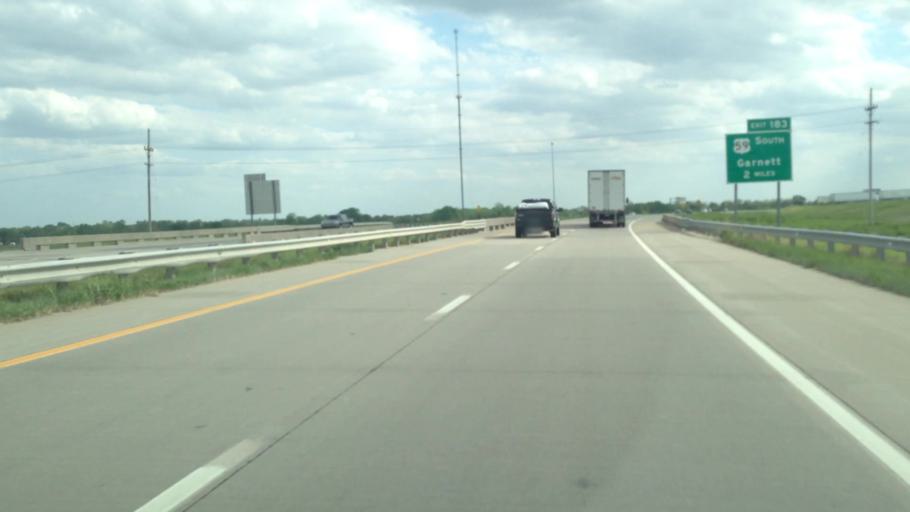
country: US
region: Kansas
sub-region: Franklin County
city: Ottawa
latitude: 38.5950
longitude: -95.2339
